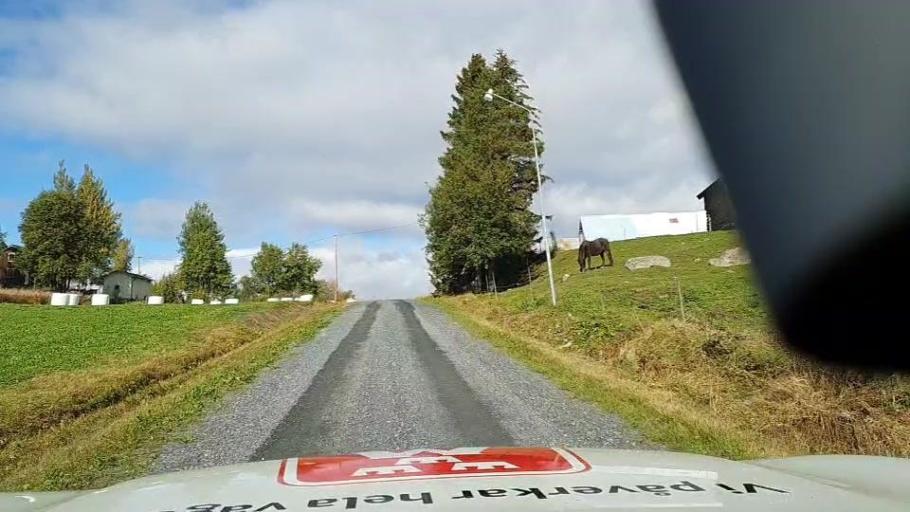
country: SE
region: Jaemtland
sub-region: Are Kommun
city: Jarpen
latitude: 63.2314
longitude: 13.6839
